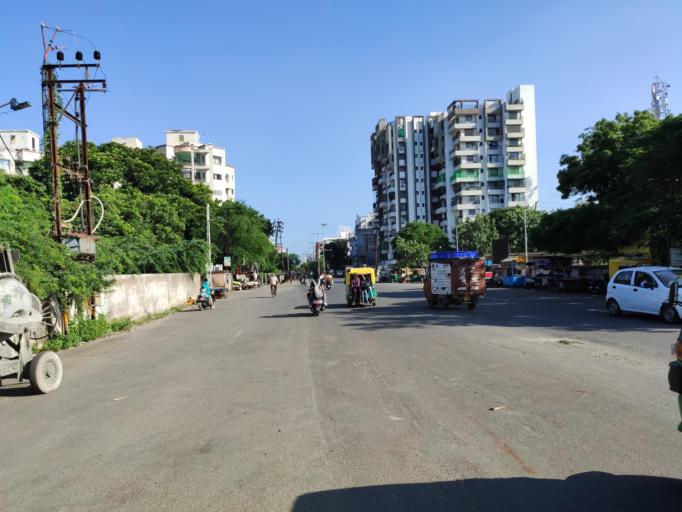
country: IN
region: Gujarat
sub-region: Jamnagar
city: Bedi
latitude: 22.4888
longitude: 70.0520
